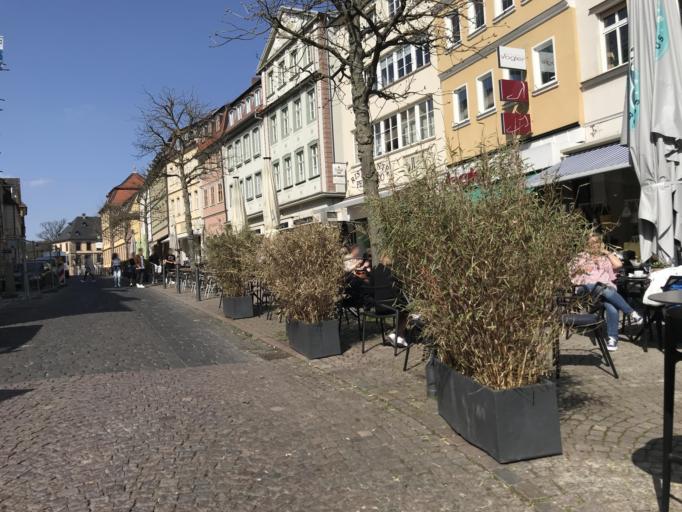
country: DE
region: Hesse
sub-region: Regierungsbezirk Kassel
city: Fulda
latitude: 50.5517
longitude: 9.6759
